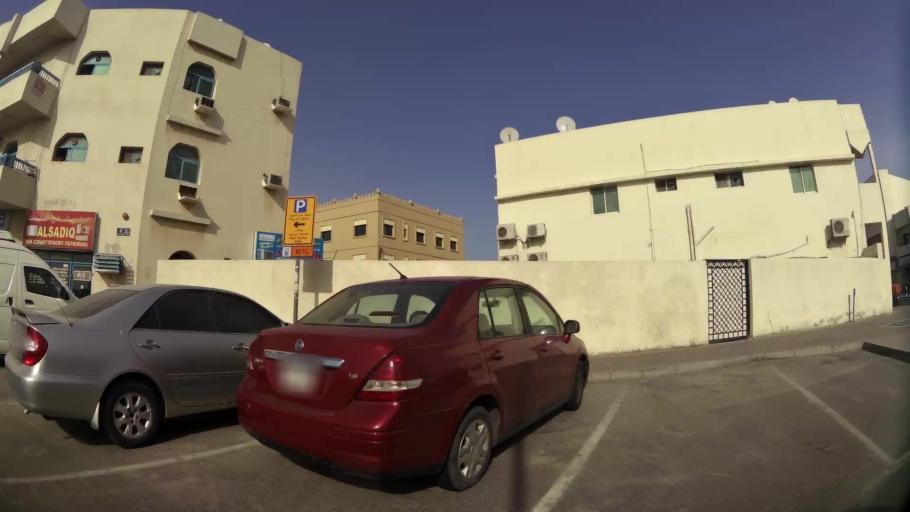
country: AE
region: Ash Shariqah
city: Sharjah
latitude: 25.2797
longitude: 55.3344
